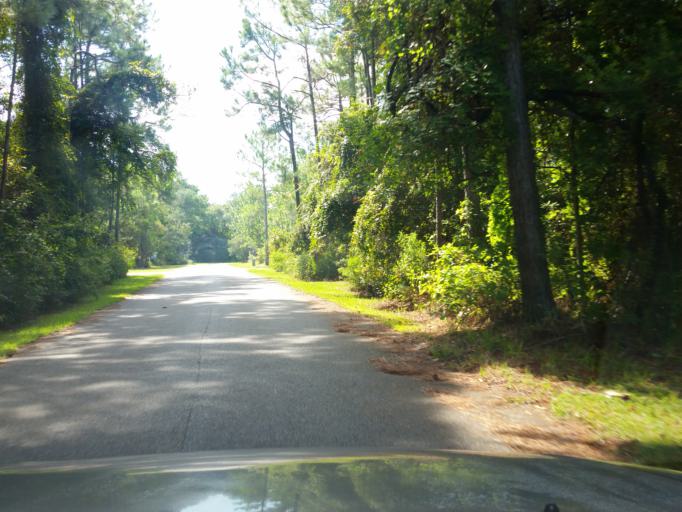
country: US
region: Alabama
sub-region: Baldwin County
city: Orange Beach
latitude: 30.3177
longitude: -87.4866
